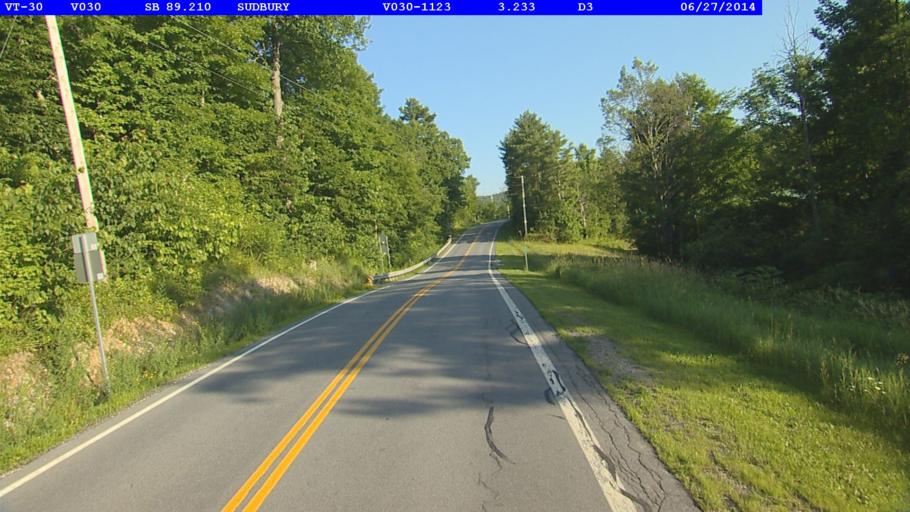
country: US
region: Vermont
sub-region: Rutland County
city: Brandon
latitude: 43.7945
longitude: -73.2053
